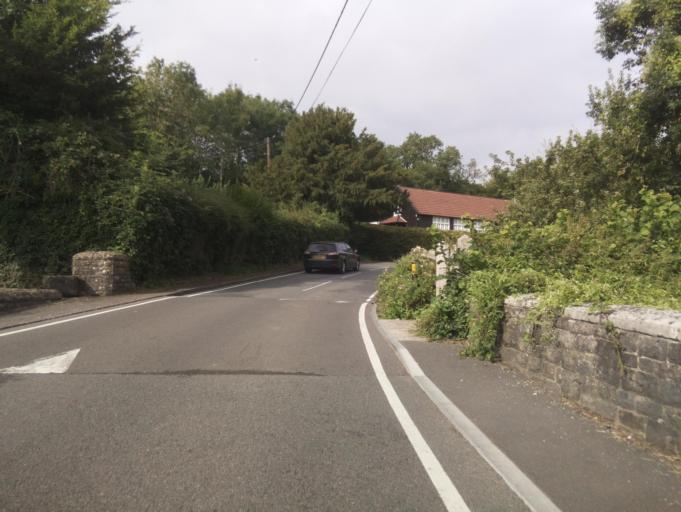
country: GB
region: England
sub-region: North Somerset
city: Long Ashton
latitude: 51.4079
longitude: -2.6750
